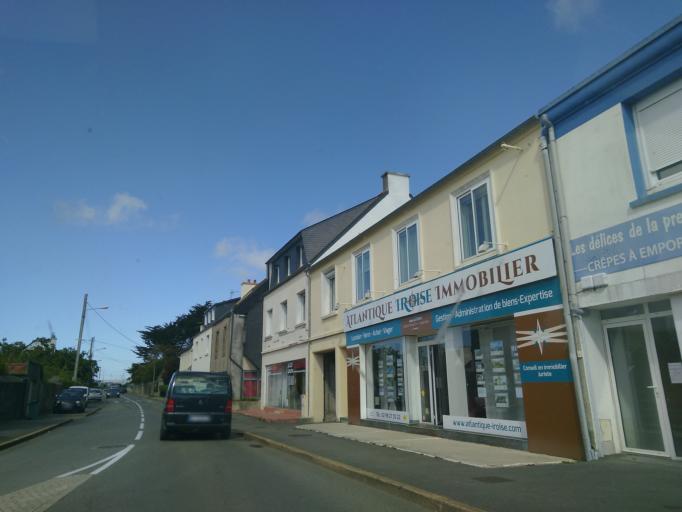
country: FR
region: Brittany
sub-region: Departement du Finistere
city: Crozon
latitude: 48.2463
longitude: -4.4957
